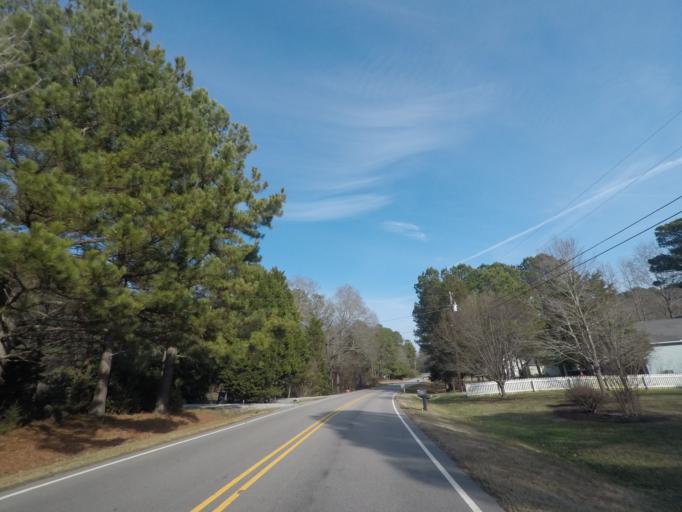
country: US
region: North Carolina
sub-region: Durham County
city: Durham
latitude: 36.0780
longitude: -78.9485
